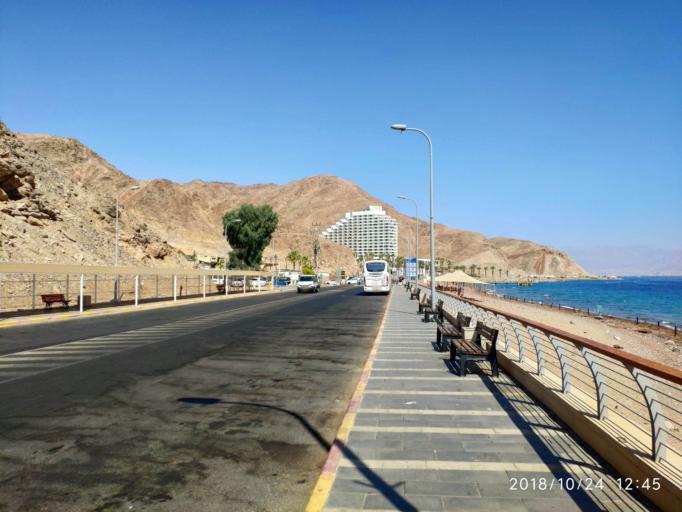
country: IL
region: Southern District
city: Eilat
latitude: 29.4927
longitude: 34.9049
